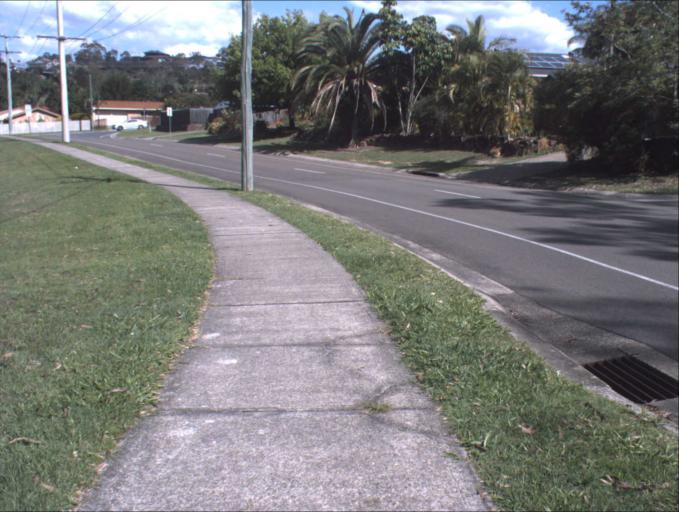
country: AU
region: Queensland
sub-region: Logan
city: Waterford West
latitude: -27.7002
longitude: 153.1611
